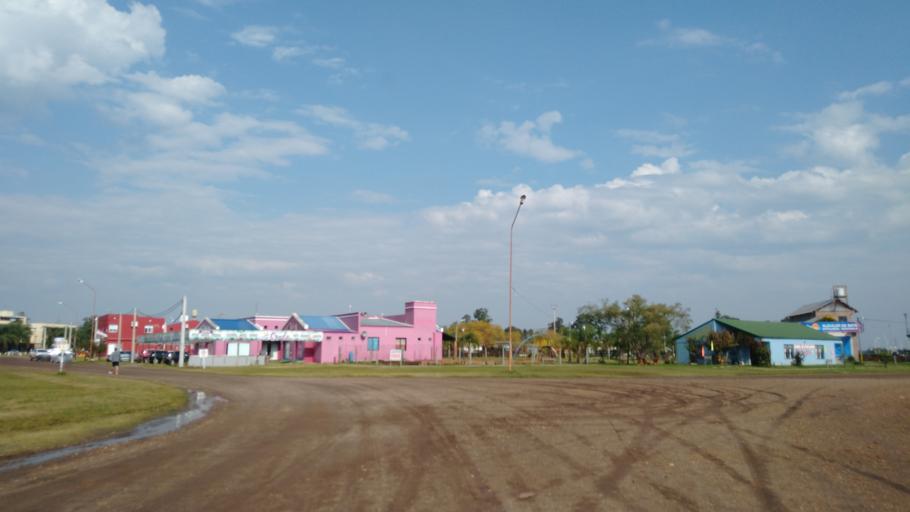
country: AR
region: Entre Rios
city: Chajari
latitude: -30.7437
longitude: -58.0117
